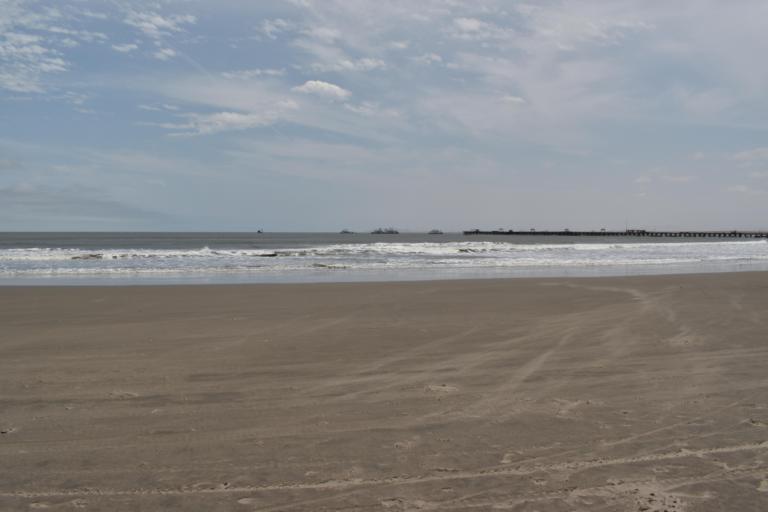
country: PE
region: La Libertad
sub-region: Ascope
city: Paijan
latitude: -7.7005
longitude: -79.4389
